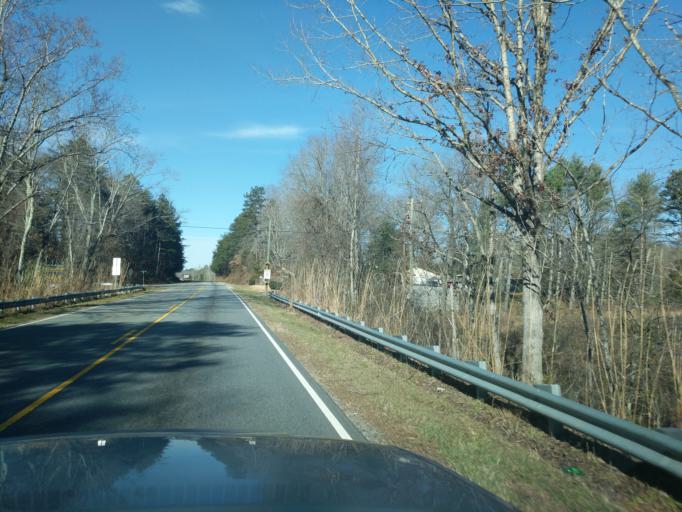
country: US
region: North Carolina
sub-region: Rutherford County
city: Rutherfordton
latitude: 35.3970
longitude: -81.9630
